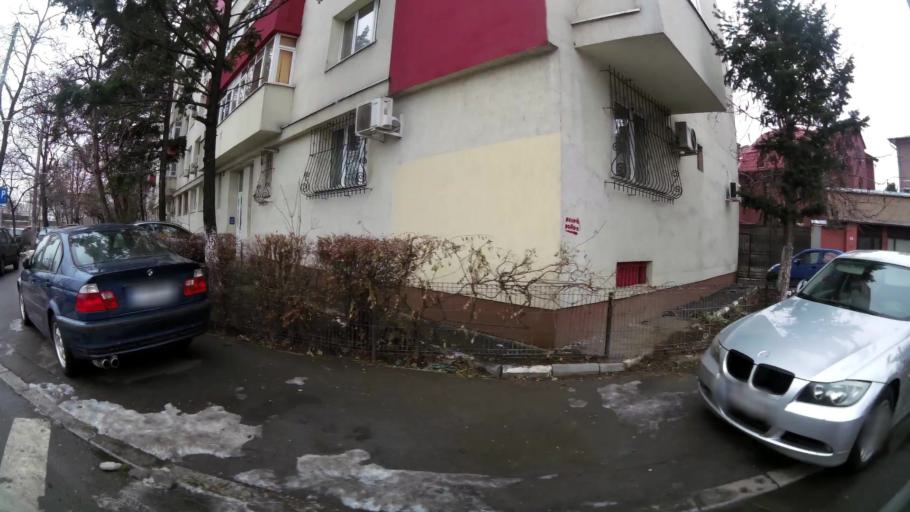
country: RO
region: Bucuresti
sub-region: Municipiul Bucuresti
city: Bucuresti
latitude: 44.4482
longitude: 26.0701
